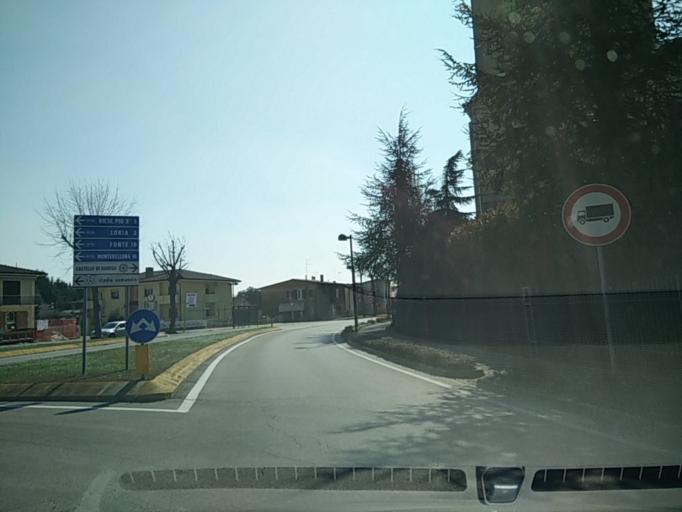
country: IT
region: Veneto
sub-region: Provincia di Treviso
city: Castello di Godego
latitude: 45.6964
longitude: 11.8757
